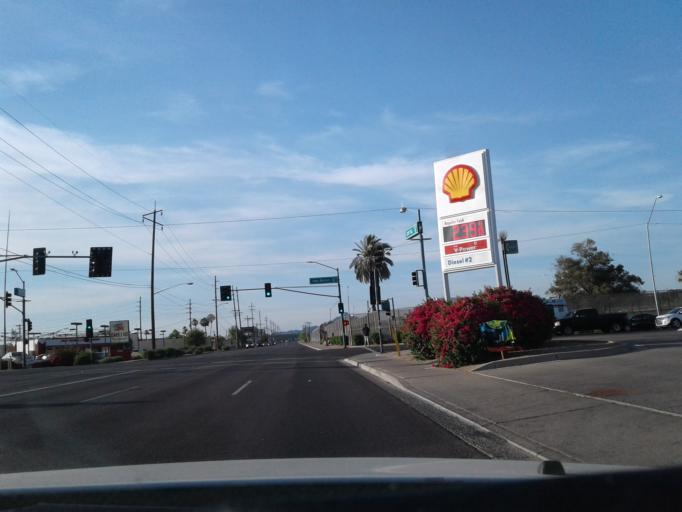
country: US
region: Arizona
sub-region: Maricopa County
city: Phoenix
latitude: 33.4509
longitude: -112.0301
